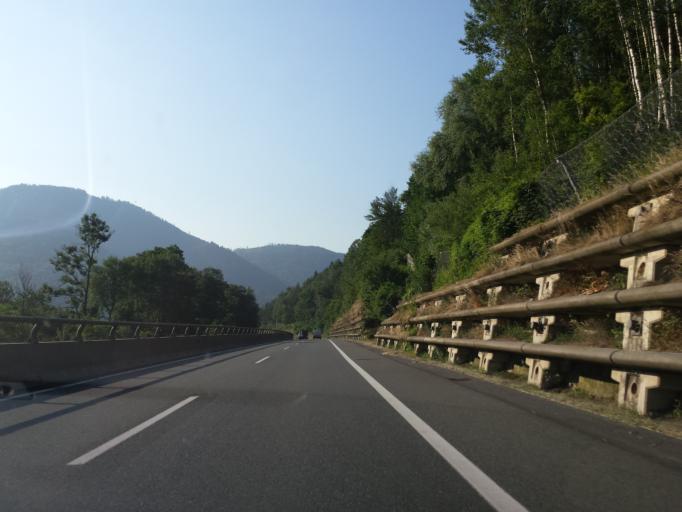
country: AT
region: Styria
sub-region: Politischer Bezirk Graz-Umgebung
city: Rothelstein
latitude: 47.3200
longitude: 15.3666
